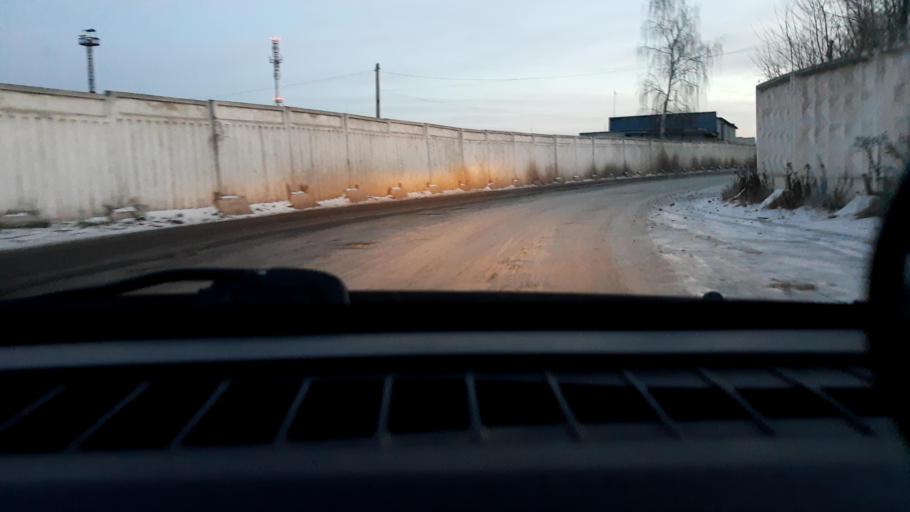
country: RU
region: Nizjnij Novgorod
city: Gorbatovka
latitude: 56.2783
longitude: 43.8398
